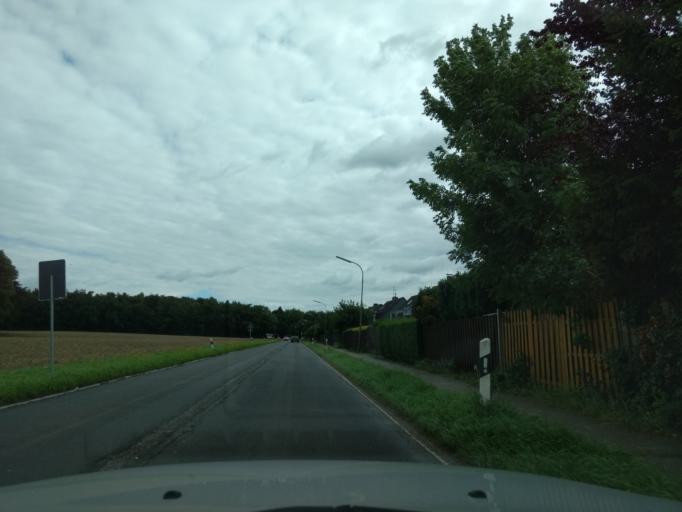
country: DE
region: North Rhine-Westphalia
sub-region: Regierungsbezirk Dusseldorf
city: Ratingen
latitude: 51.3186
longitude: 6.8862
